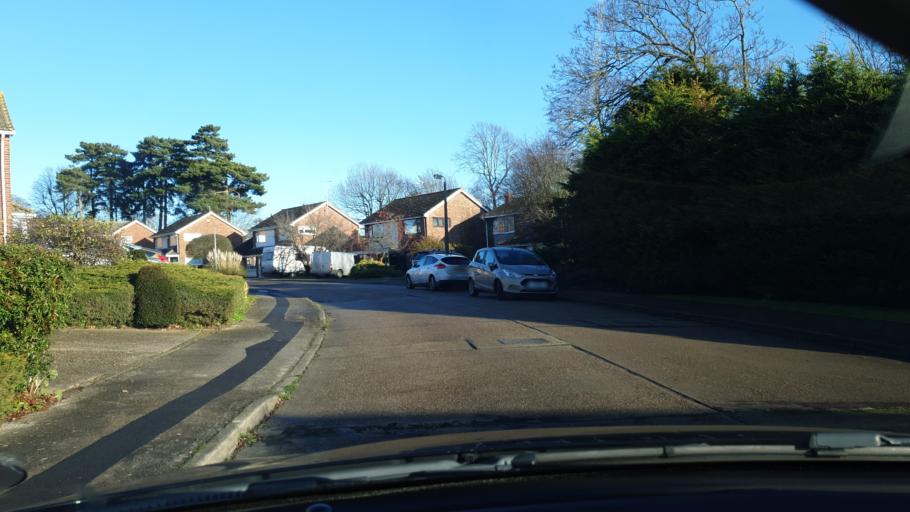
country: GB
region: England
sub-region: Essex
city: Brightlingsea
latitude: 51.8164
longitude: 1.0199
